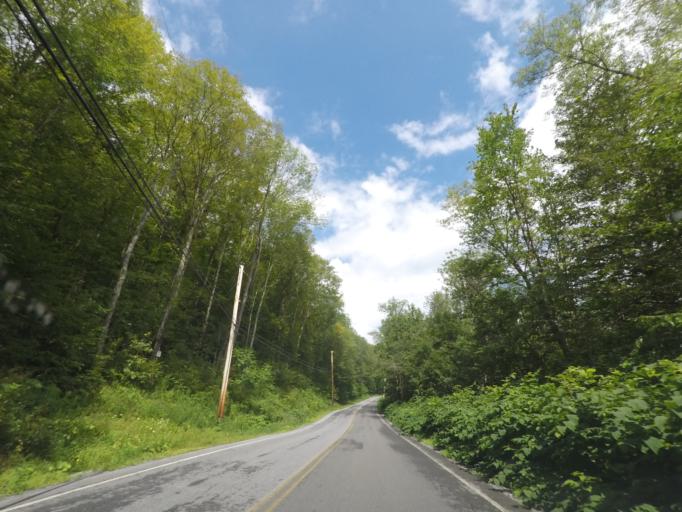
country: US
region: New York
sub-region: Rensselaer County
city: Averill Park
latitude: 42.6920
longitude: -73.3898
